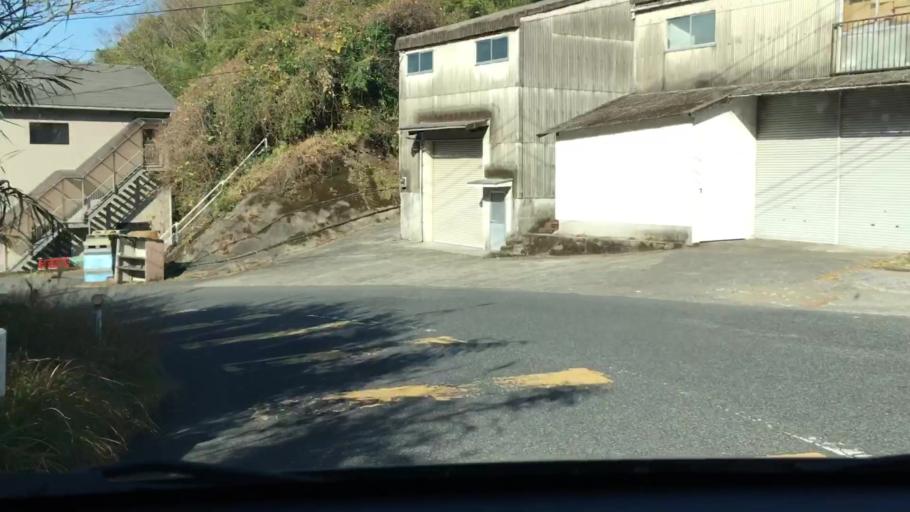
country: JP
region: Kagoshima
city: Kokubu-matsuki
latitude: 31.6706
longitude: 130.8227
